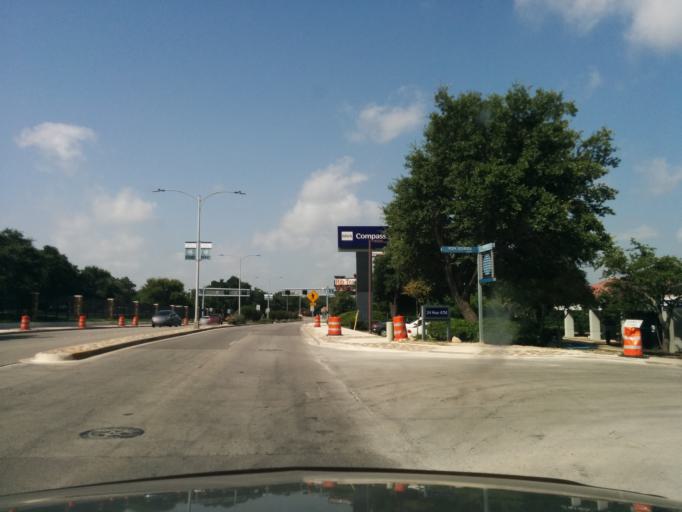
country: US
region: Texas
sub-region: Bexar County
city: Balcones Heights
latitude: 29.5075
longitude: -98.5815
